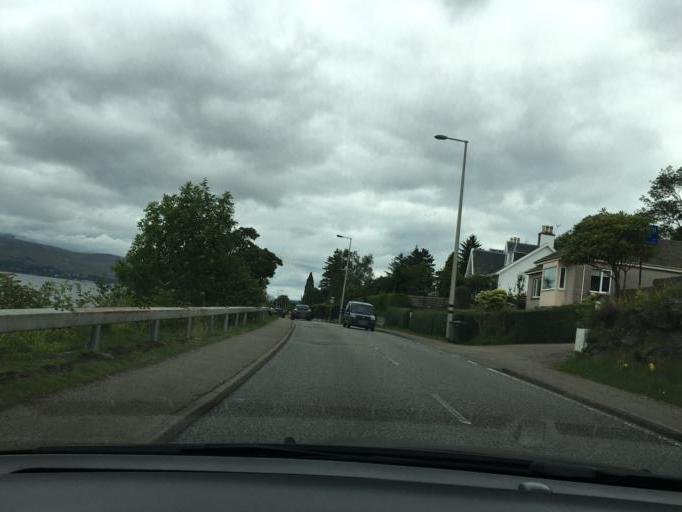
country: GB
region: Scotland
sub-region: Highland
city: Fort William
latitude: 56.8063
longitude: -5.1292
